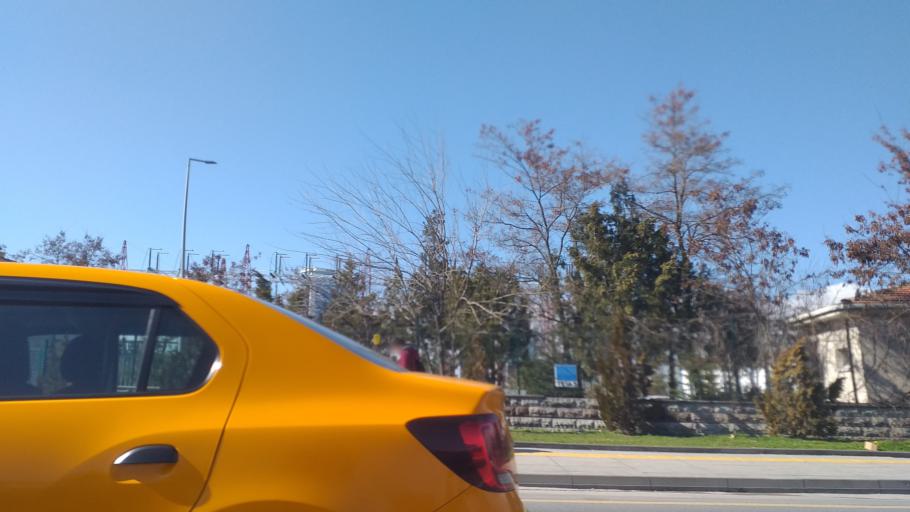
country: TR
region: Ankara
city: Ankara
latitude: 39.9150
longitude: 32.8141
